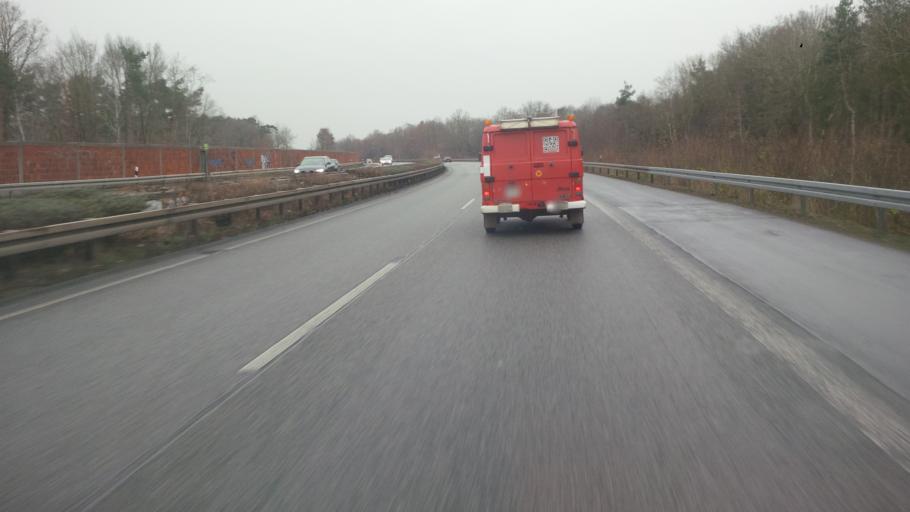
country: DE
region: Hesse
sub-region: Regierungsbezirk Giessen
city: Giessen
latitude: 50.5815
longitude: 8.7117
